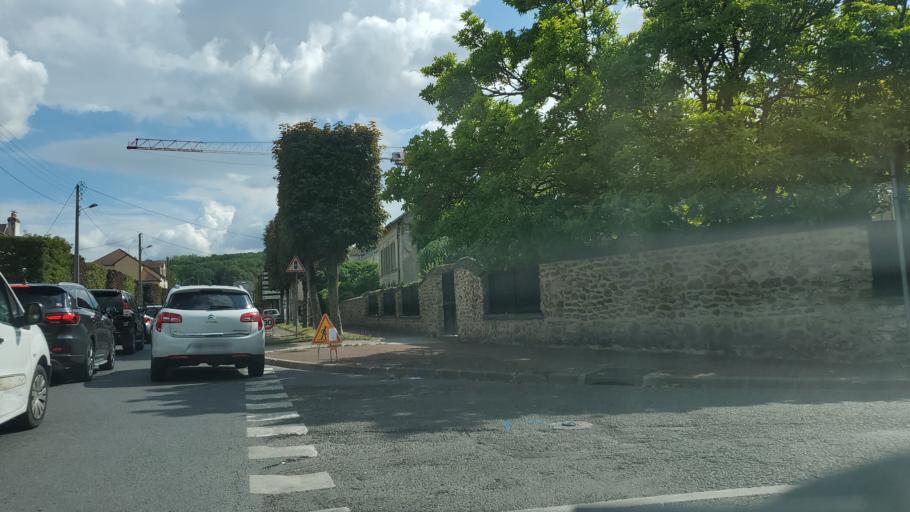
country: FR
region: Ile-de-France
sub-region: Departement de Seine-et-Marne
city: Coulommiers
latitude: 48.8047
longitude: 3.0848
